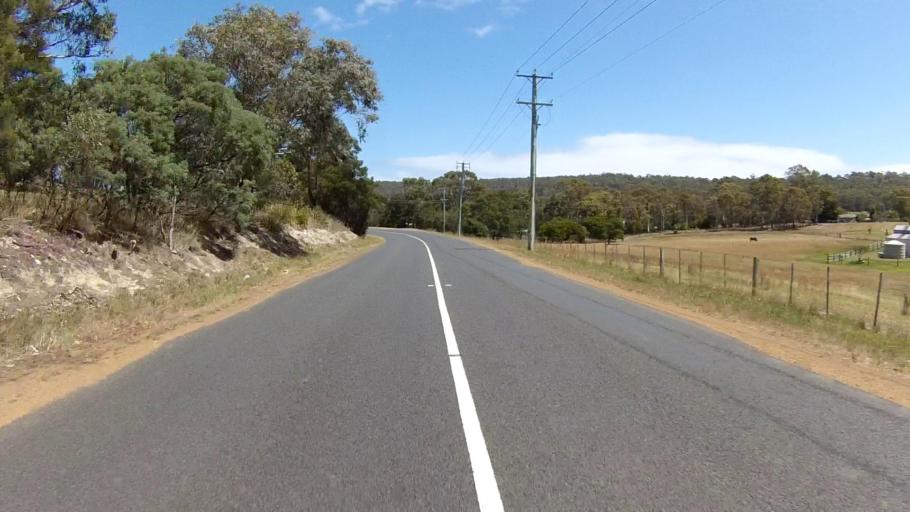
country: AU
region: Tasmania
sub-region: Clarence
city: Sandford
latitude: -42.9567
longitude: 147.4765
